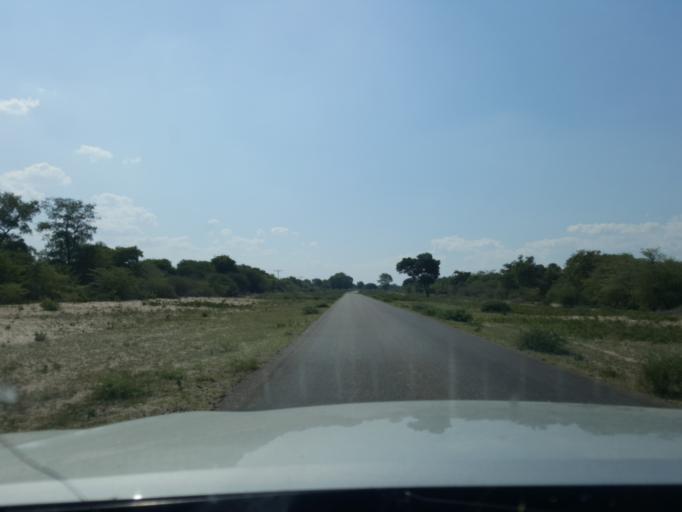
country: BW
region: North West
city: Shakawe
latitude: -18.7863
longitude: 22.1947
